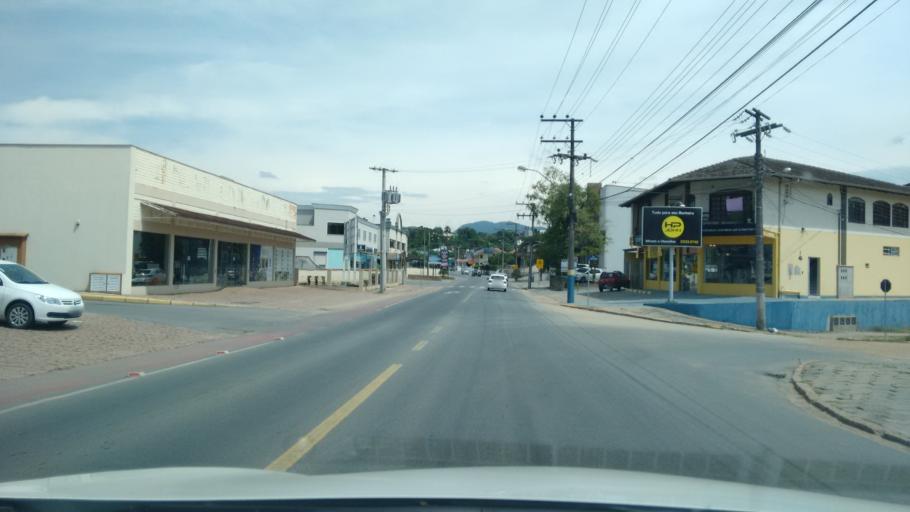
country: BR
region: Santa Catarina
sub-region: Timbo
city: Timbo
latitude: -26.8355
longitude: -49.2721
